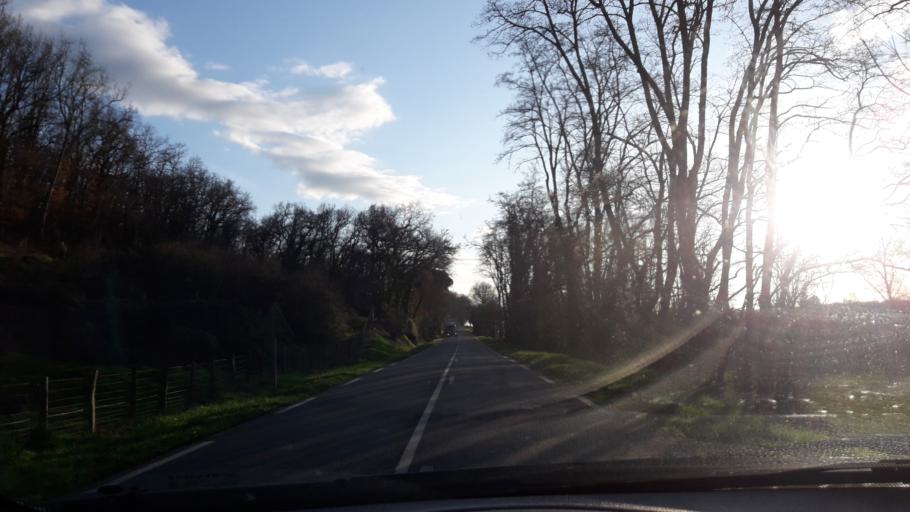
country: FR
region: Midi-Pyrenees
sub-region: Departement de la Haute-Garonne
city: Daux
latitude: 43.7331
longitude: 1.2559
